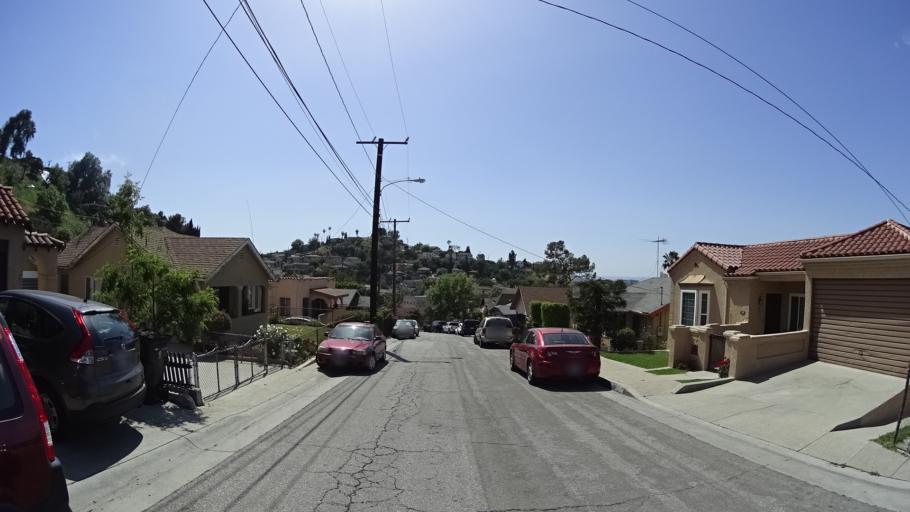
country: US
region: California
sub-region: Los Angeles County
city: Belvedere
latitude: 34.0542
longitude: -118.1861
